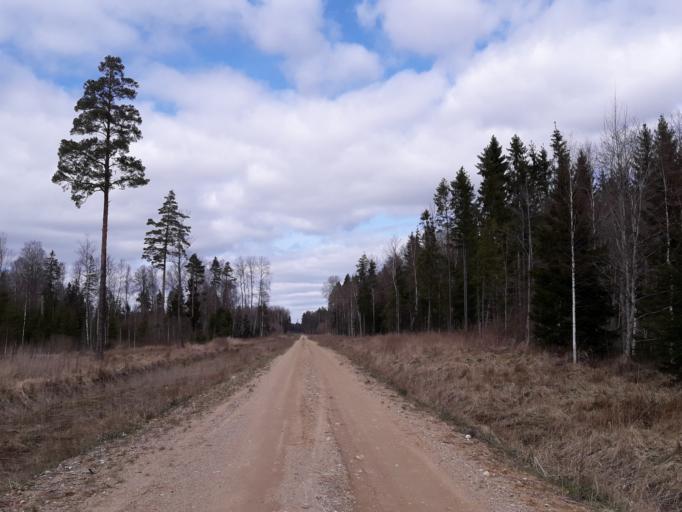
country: LV
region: Talsu Rajons
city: Sabile
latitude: 56.8960
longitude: 22.3791
